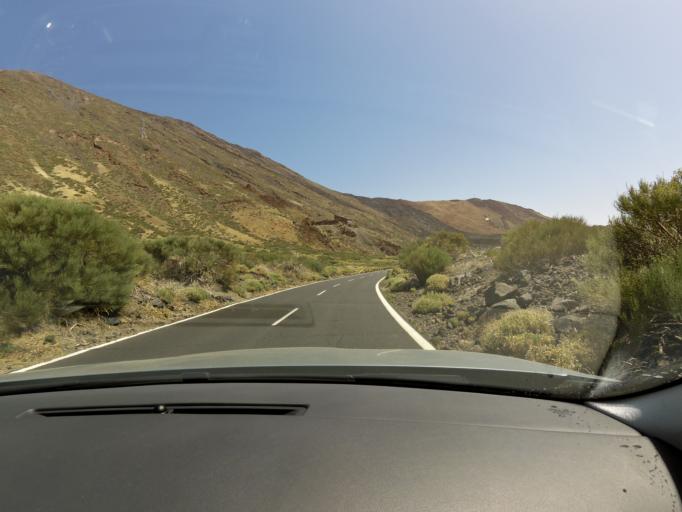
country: ES
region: Canary Islands
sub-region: Provincia de Santa Cruz de Tenerife
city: Vilaflor
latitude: 28.2502
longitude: -16.6272
